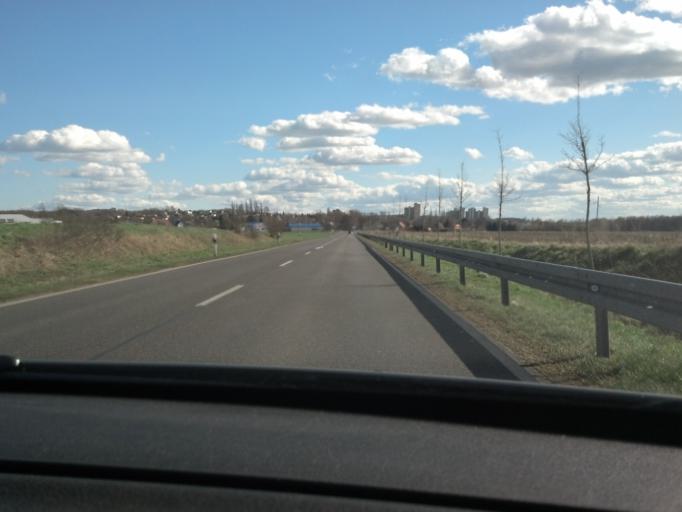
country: DE
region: Mecklenburg-Vorpommern
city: Trollenhagen
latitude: 53.5969
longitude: 13.2717
